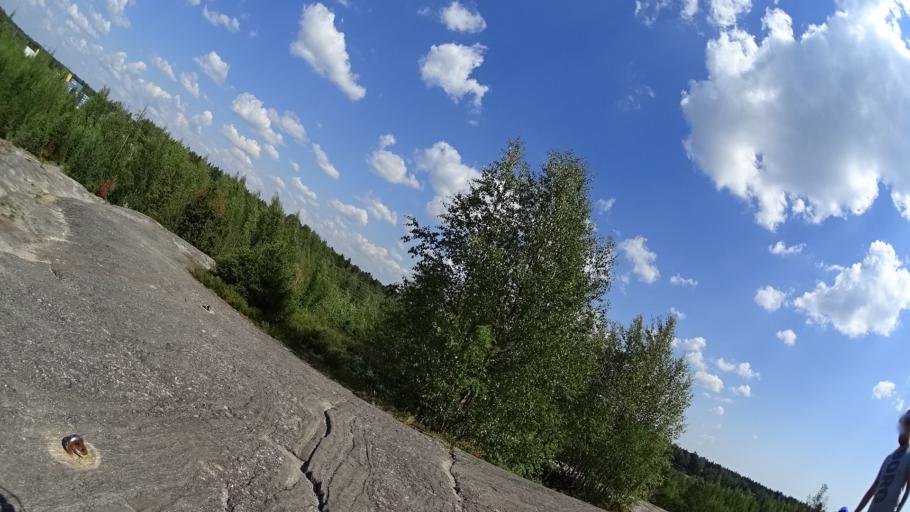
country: FI
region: Uusimaa
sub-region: Helsinki
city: Vantaa
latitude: 60.3387
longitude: 24.9945
